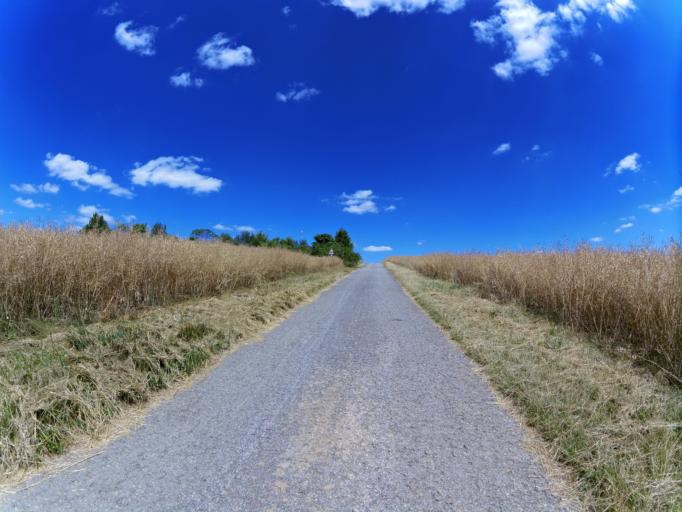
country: DE
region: Bavaria
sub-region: Regierungsbezirk Unterfranken
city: Retzstadt
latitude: 49.8928
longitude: 9.8720
